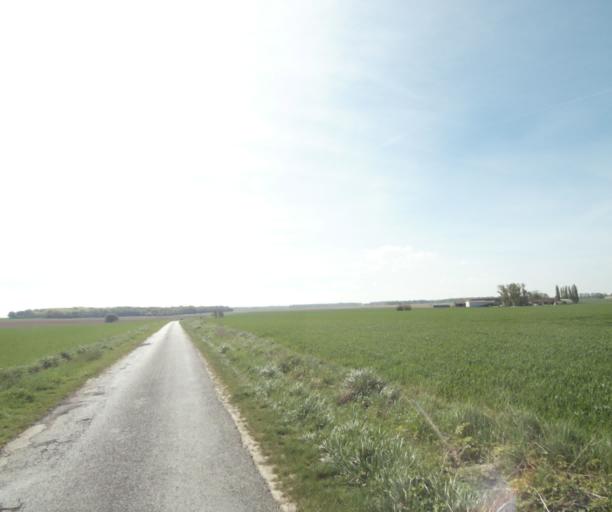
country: FR
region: Ile-de-France
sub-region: Departement de Seine-et-Marne
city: Nangis
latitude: 48.5500
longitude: 3.0329
